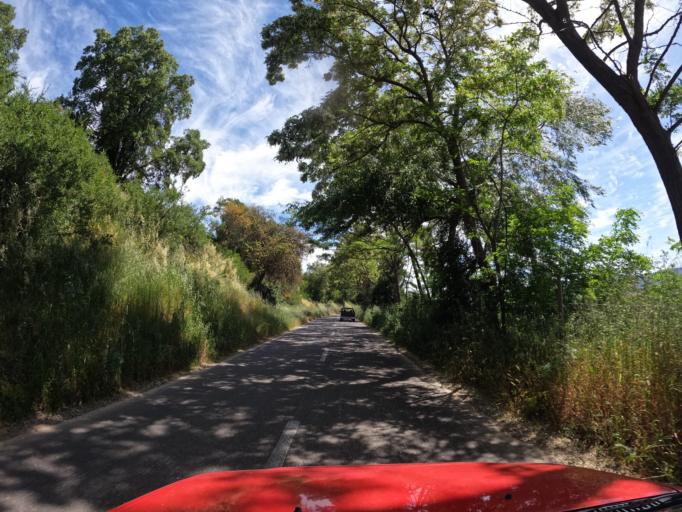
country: CL
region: Maule
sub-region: Provincia de Talca
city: Talca
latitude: -34.9892
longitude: -71.8316
